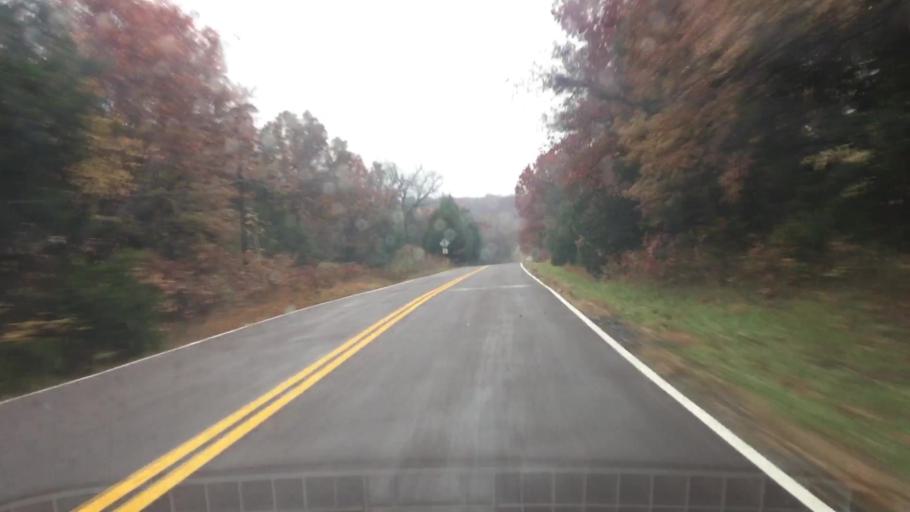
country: US
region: Missouri
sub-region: Boone County
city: Columbia
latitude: 38.8720
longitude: -92.3233
